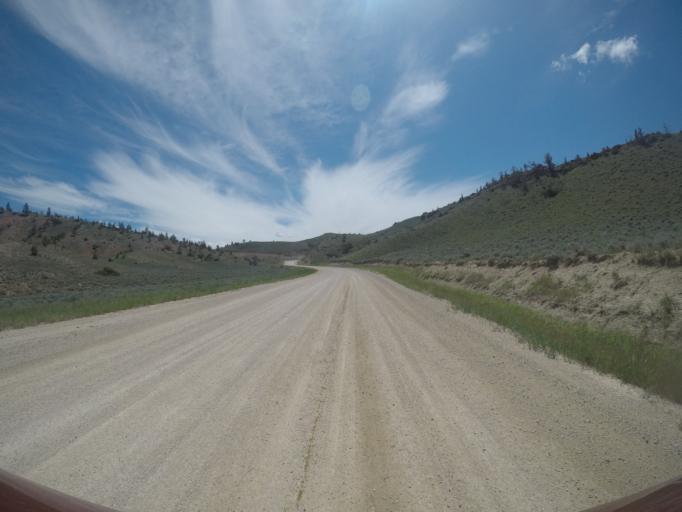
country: US
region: Montana
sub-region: Carbon County
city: Red Lodge
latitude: 45.2081
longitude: -108.8025
